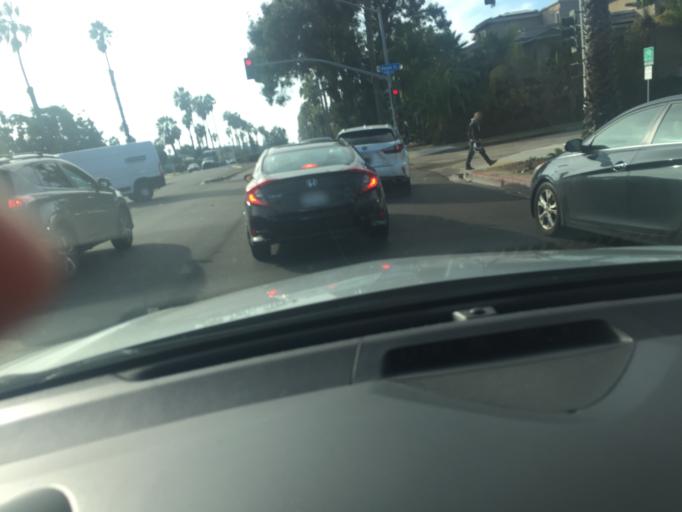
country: US
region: California
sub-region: San Diego County
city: San Diego
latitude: 32.7865
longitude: -117.1920
